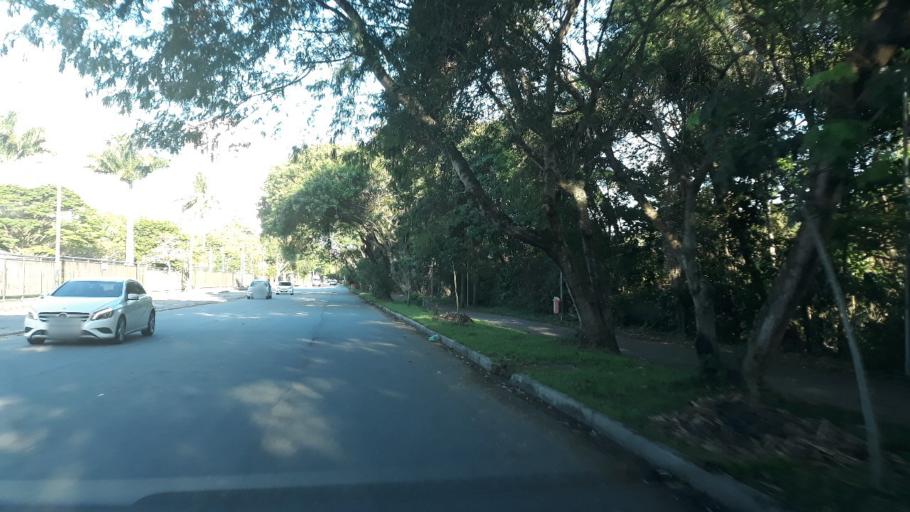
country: BR
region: Rio de Janeiro
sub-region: Rio De Janeiro
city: Rio de Janeiro
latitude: -23.0059
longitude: -43.3439
